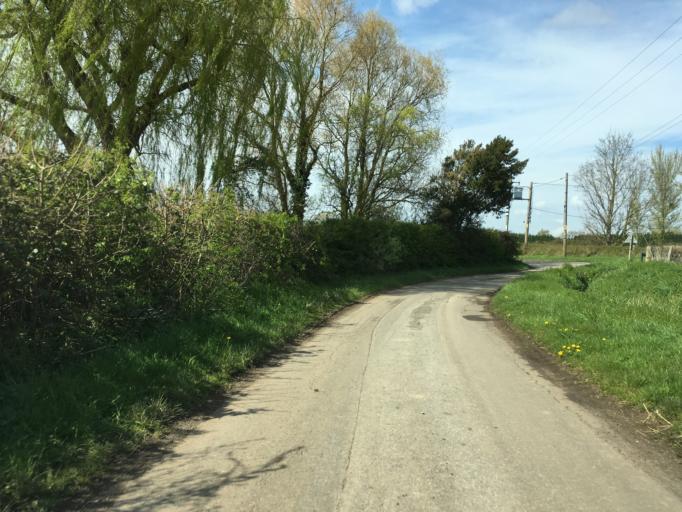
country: GB
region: England
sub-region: South Gloucestershire
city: Almondsbury
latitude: 51.5690
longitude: -2.5866
